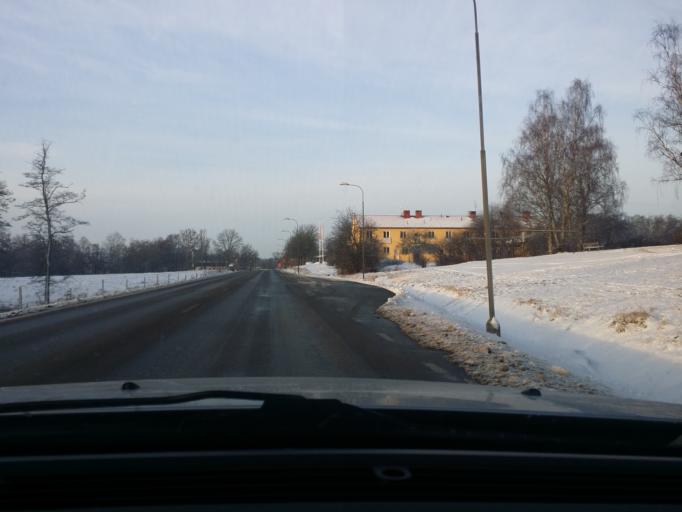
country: SE
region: OErebro
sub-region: Lindesbergs Kommun
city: Lindesberg
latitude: 59.5261
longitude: 15.2919
